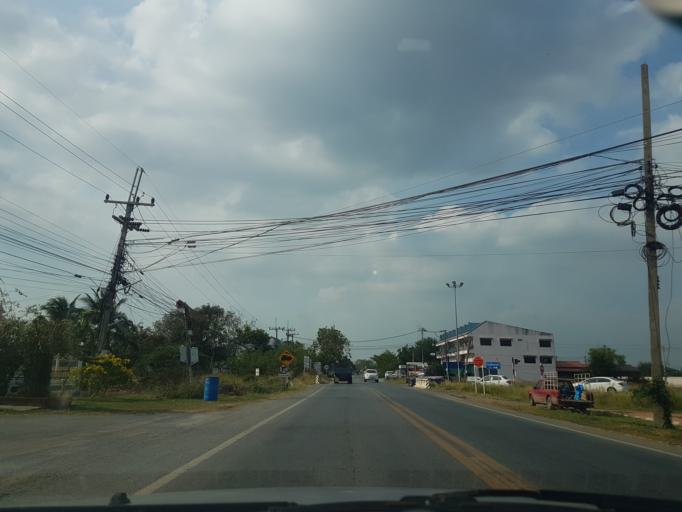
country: TH
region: Phra Nakhon Si Ayutthaya
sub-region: Amphoe Tha Ruea
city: Tha Ruea
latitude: 14.5518
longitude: 100.7263
